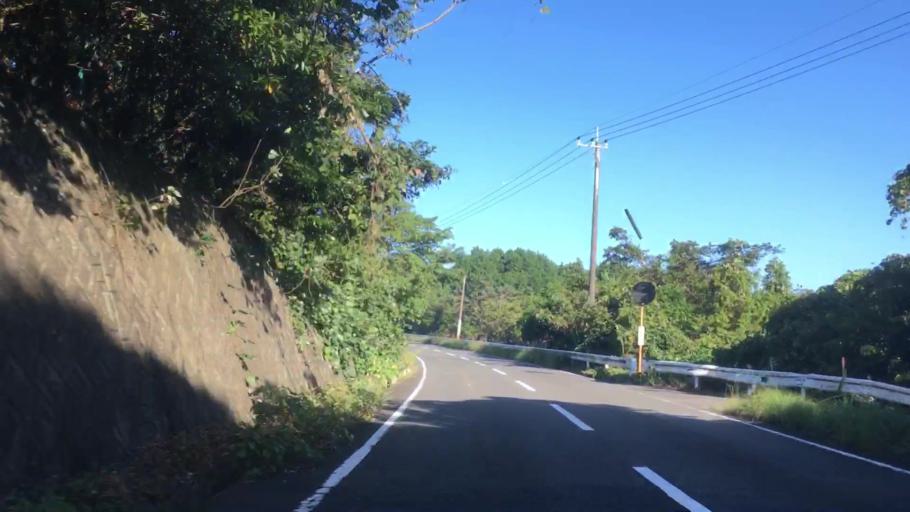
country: JP
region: Nagasaki
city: Sasebo
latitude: 33.0313
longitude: 129.6894
